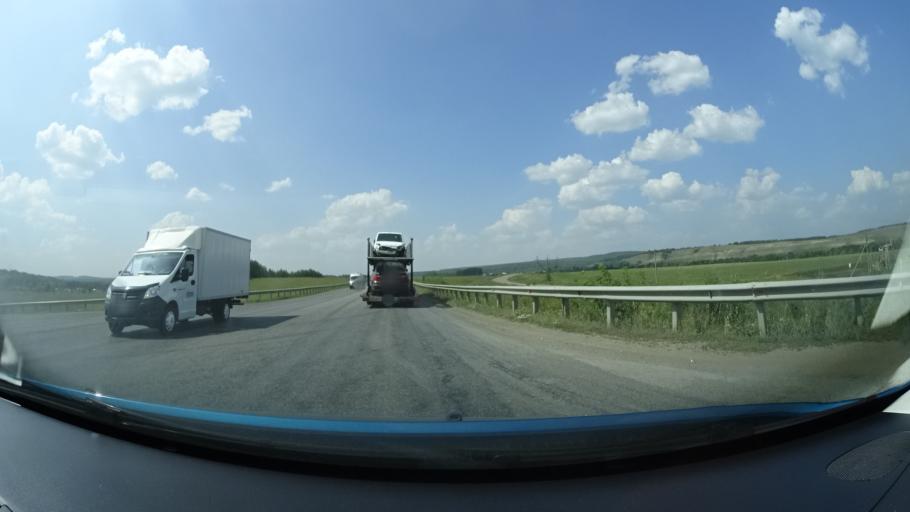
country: RU
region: Bashkortostan
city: Nizhnetroitskiy
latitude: 54.4560
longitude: 53.6770
